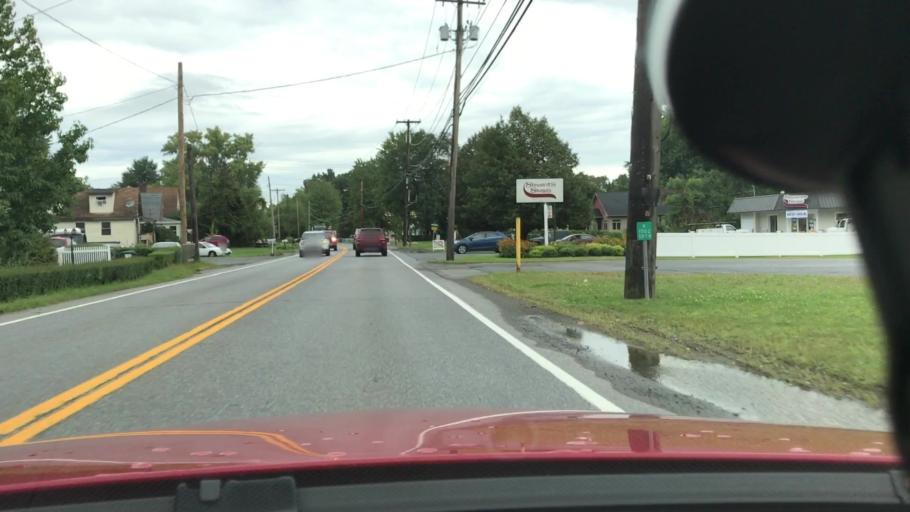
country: US
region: New York
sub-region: Saratoga County
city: Waterford
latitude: 42.8045
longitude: -73.6677
